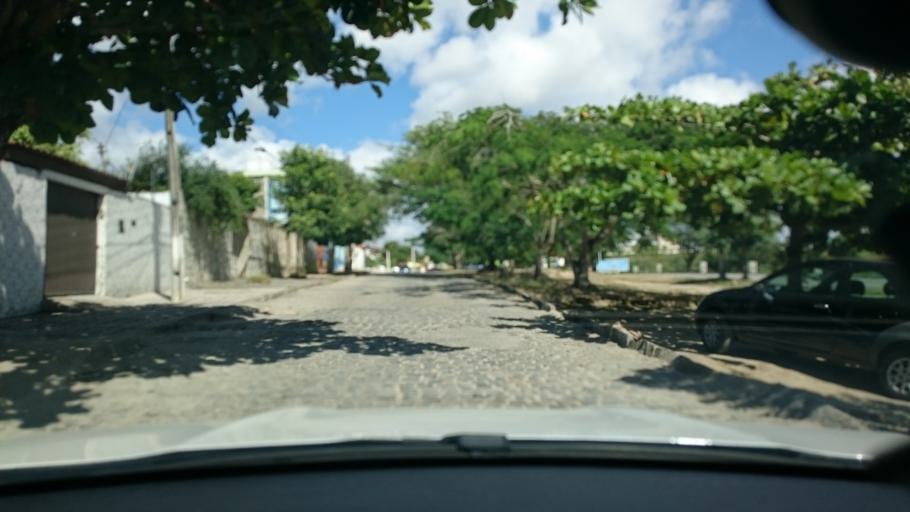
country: BR
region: Paraiba
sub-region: Campina Grande
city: Campina Grande
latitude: -7.2387
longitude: -35.9261
